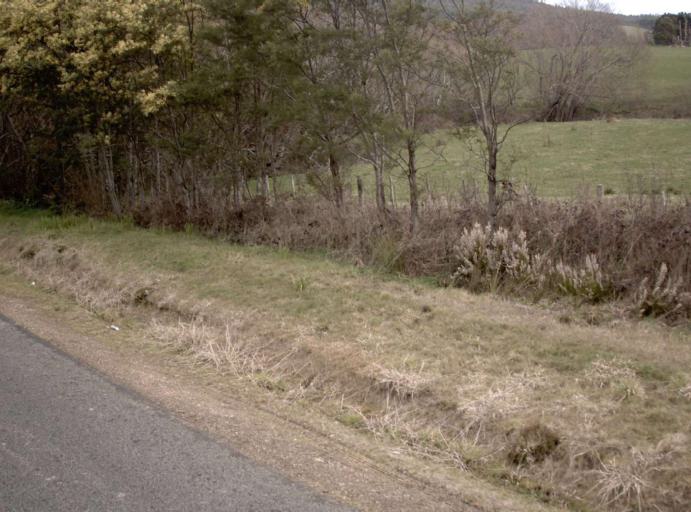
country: AU
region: Tasmania
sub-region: Launceston
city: Mayfield
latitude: -41.2061
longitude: 147.1178
